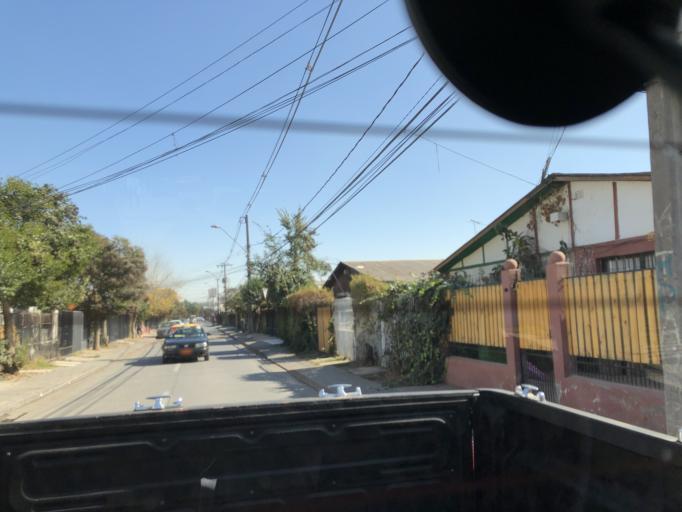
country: CL
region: Santiago Metropolitan
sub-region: Provincia de Cordillera
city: Puente Alto
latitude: -33.5676
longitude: -70.5807
